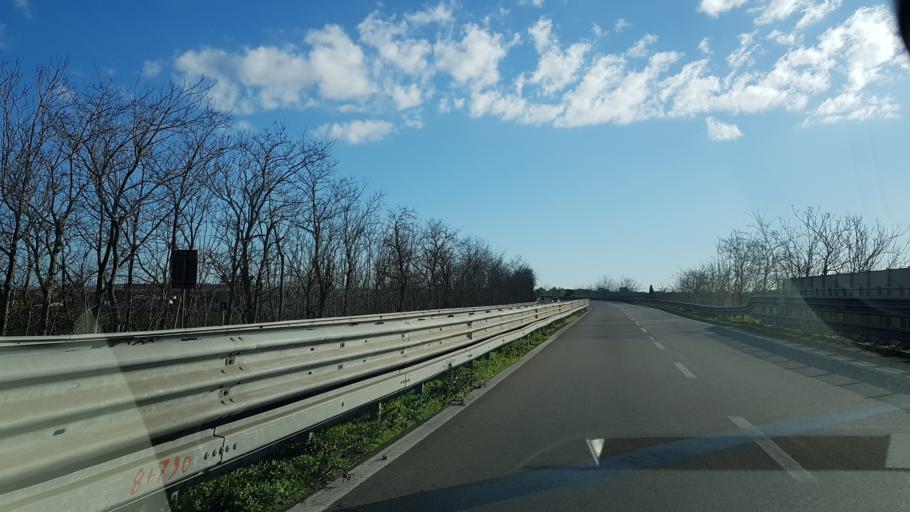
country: IT
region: Apulia
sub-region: Provincia di Lecce
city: Castromediano
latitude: 40.3240
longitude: 18.1698
